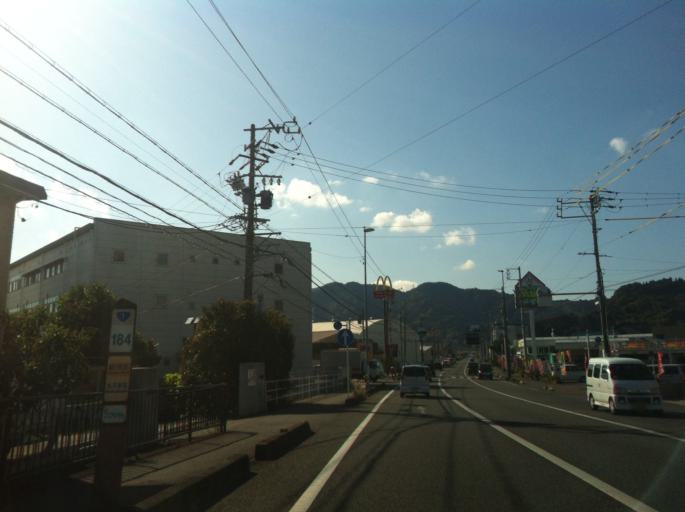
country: JP
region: Shizuoka
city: Shizuoka-shi
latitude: 34.9533
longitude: 138.3667
